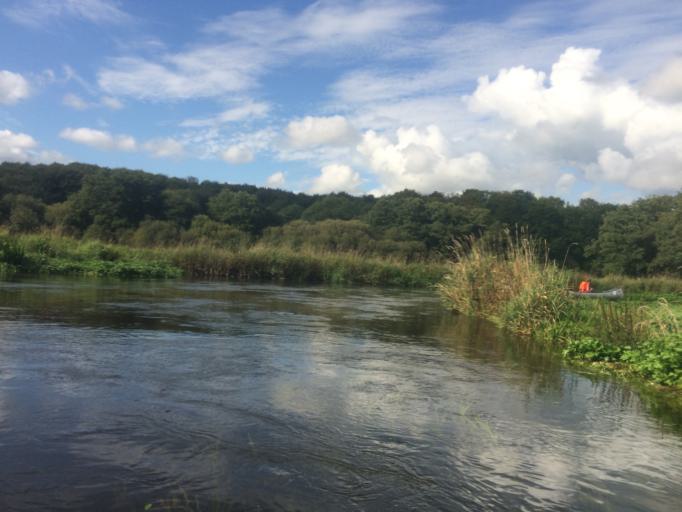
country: DK
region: South Denmark
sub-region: Vejle Kommune
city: Egtved
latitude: 55.6623
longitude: 9.3188
